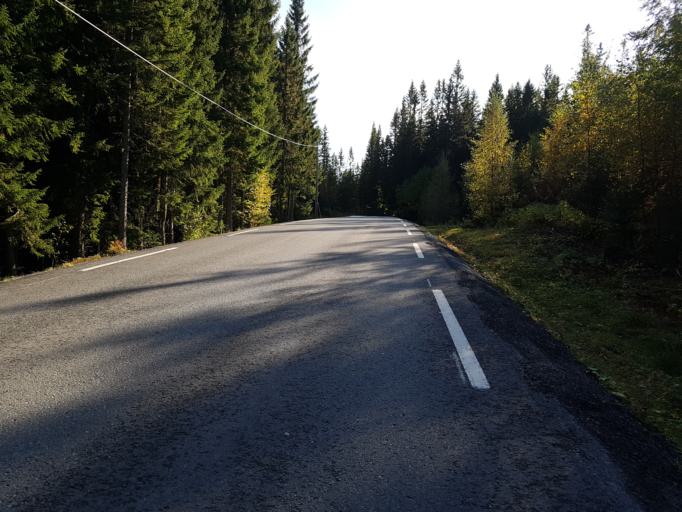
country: NO
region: Sor-Trondelag
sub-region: Malvik
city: Malvik
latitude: 63.3790
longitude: 10.6007
